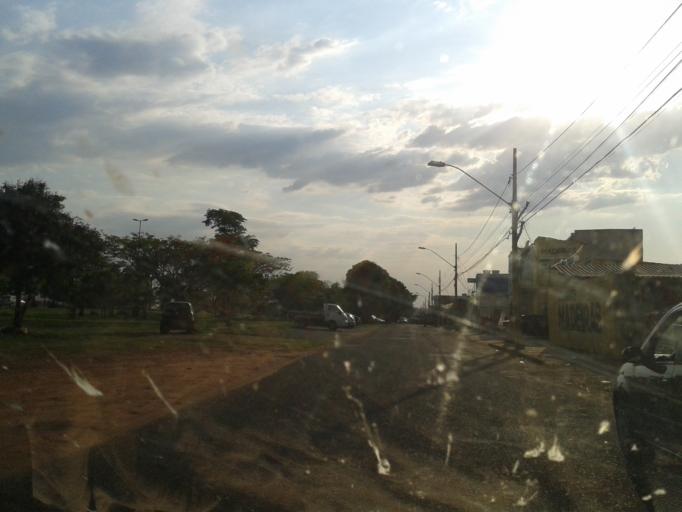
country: BR
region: Minas Gerais
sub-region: Uberlandia
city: Uberlandia
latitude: -18.9401
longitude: -48.3128
